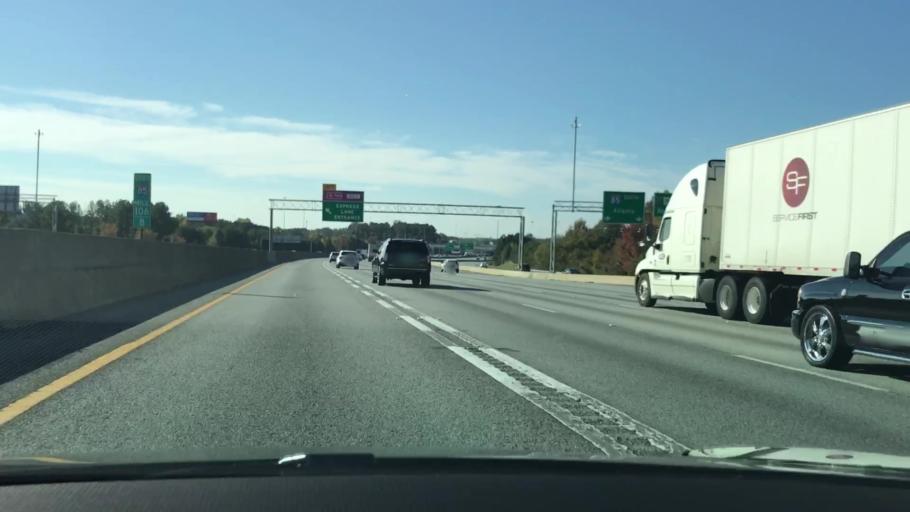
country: US
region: Georgia
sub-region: Gwinnett County
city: Duluth
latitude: 33.9739
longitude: -84.0910
